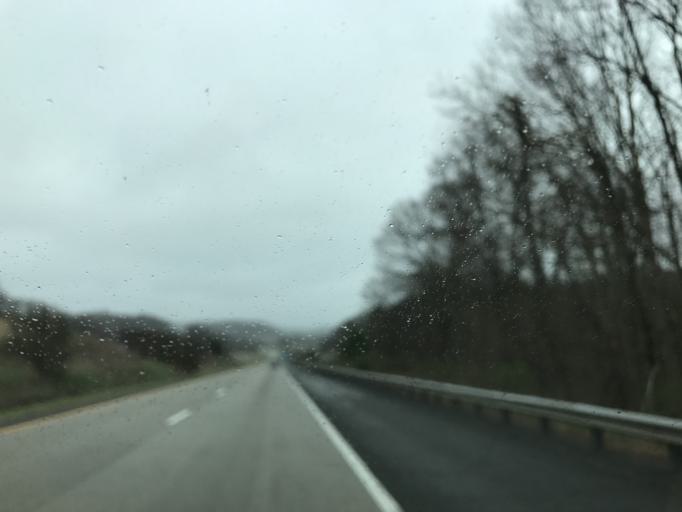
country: US
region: West Virginia
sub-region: Greenbrier County
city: Rainelle
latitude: 37.8408
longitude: -80.7456
